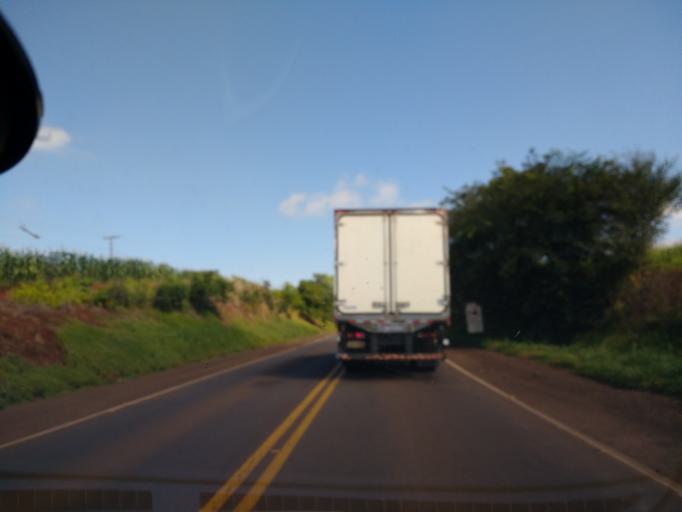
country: BR
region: Parana
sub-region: Terra Boa
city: Terra Boa
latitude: -23.5984
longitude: -52.3935
